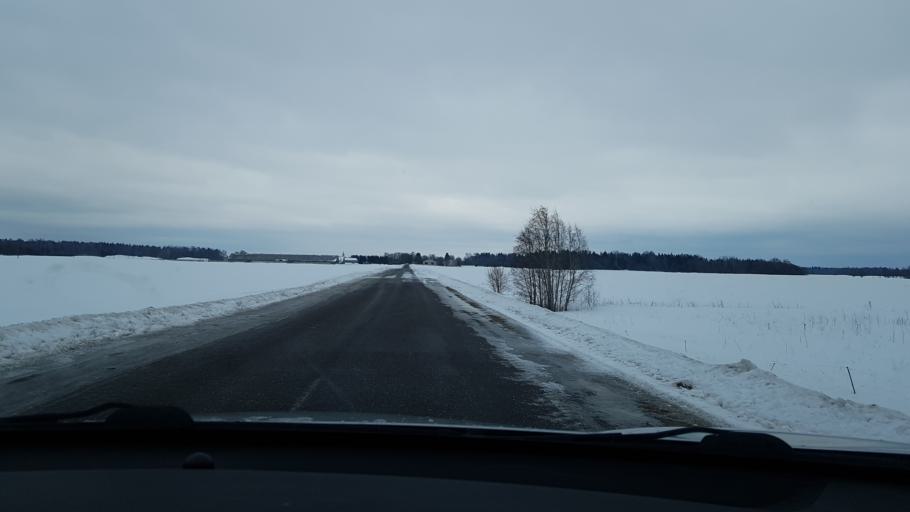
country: EE
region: Jaervamaa
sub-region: Koeru vald
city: Koeru
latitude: 58.9808
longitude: 25.9930
